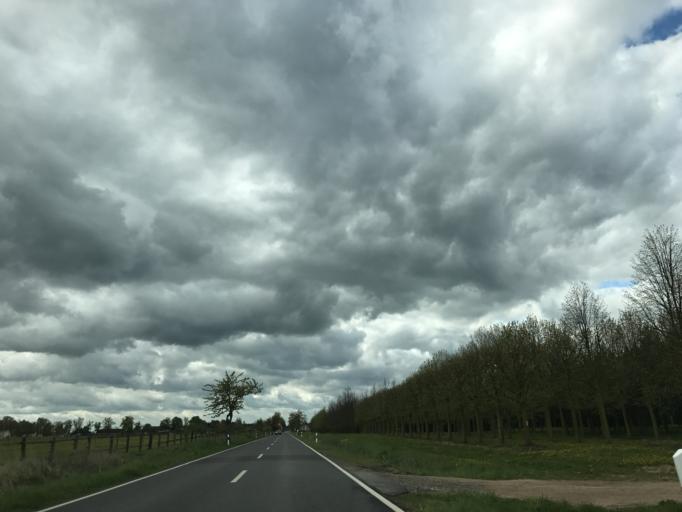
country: DE
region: Brandenburg
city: Pawesin
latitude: 52.5516
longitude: 12.7659
